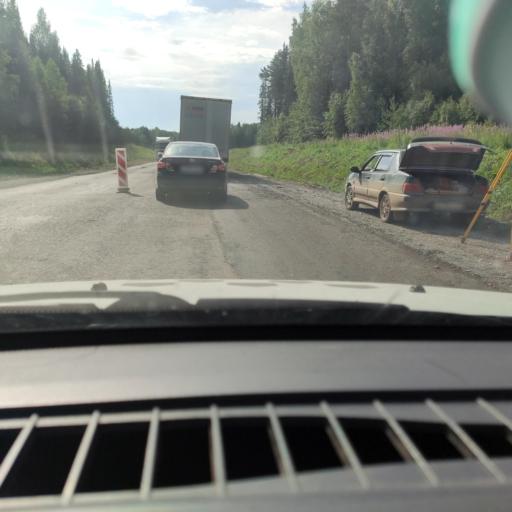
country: RU
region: Perm
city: Siva
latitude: 58.4518
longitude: 54.4188
